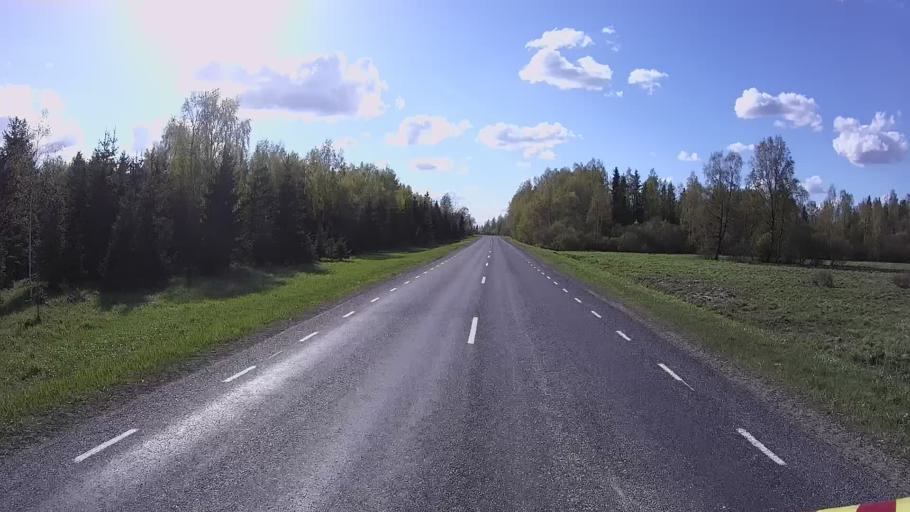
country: EE
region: Jogevamaa
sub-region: Jogeva linn
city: Jogeva
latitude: 58.7384
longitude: 26.2641
